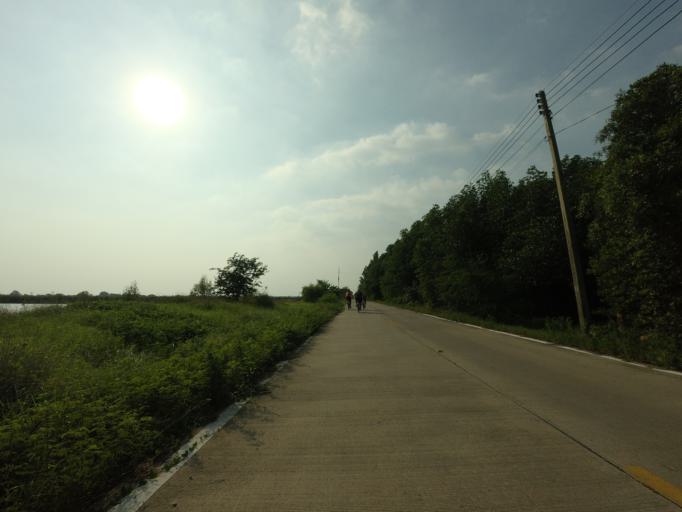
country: TH
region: Samut Sakhon
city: Samut Sakhon
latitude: 13.5080
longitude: 100.3249
